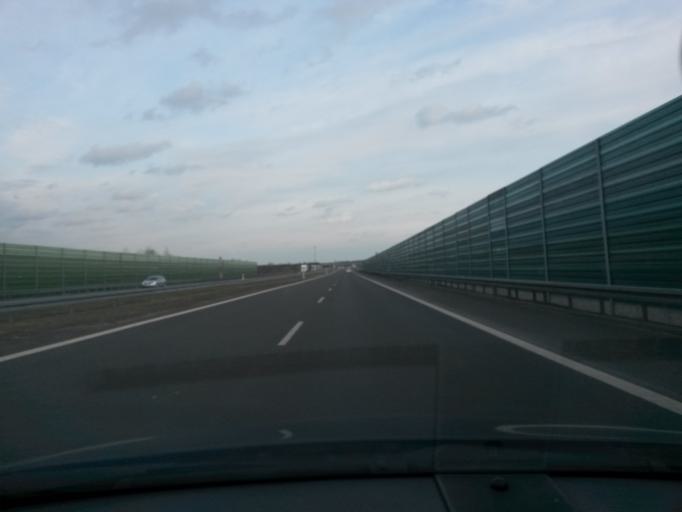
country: PL
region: Greater Poland Voivodeship
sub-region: Powiat kolski
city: Grzegorzew
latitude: 52.1204
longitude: 18.6994
